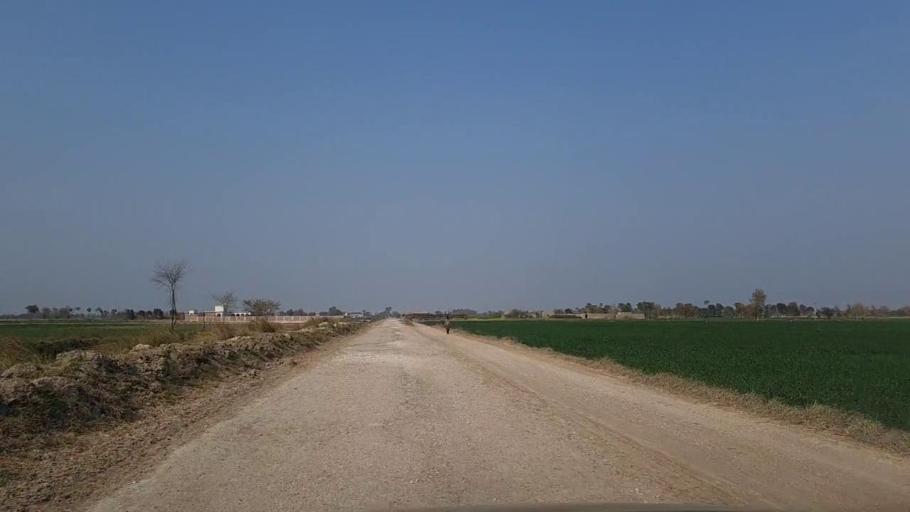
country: PK
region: Sindh
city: Daur
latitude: 26.4174
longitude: 68.4088
